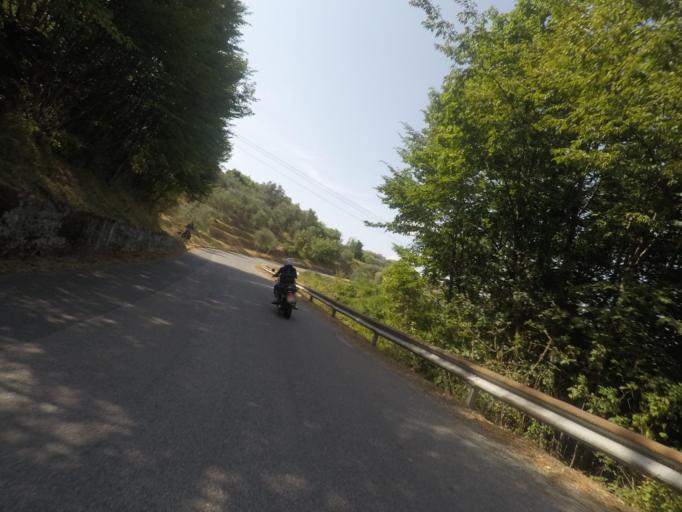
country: IT
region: Tuscany
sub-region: Provincia di Massa-Carrara
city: Fivizzano
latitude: 44.1700
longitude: 10.1018
